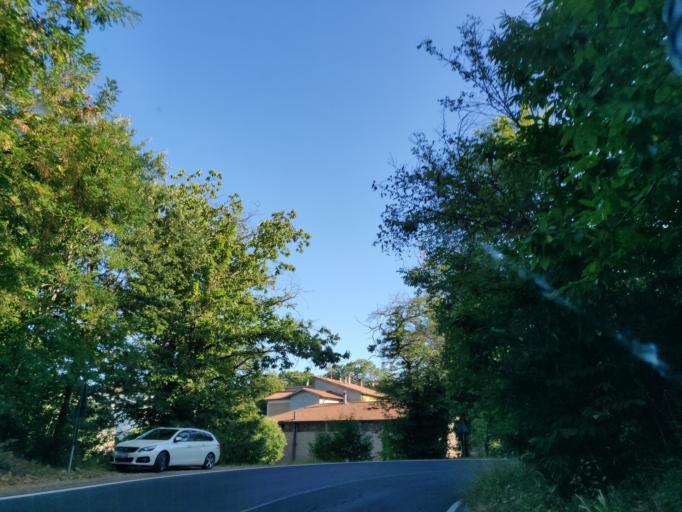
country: IT
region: Tuscany
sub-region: Provincia di Siena
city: Piancastagnaio
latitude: 42.8540
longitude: 11.6851
